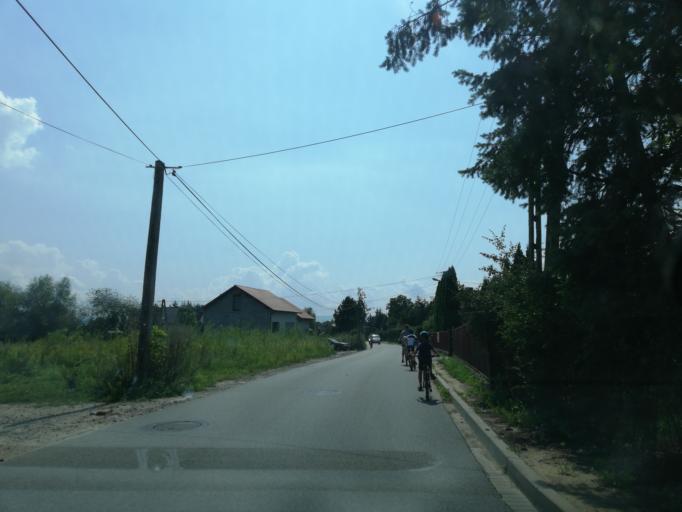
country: PL
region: Lesser Poland Voivodeship
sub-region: Powiat nowosadecki
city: Chelmiec
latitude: 49.6390
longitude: 20.6780
